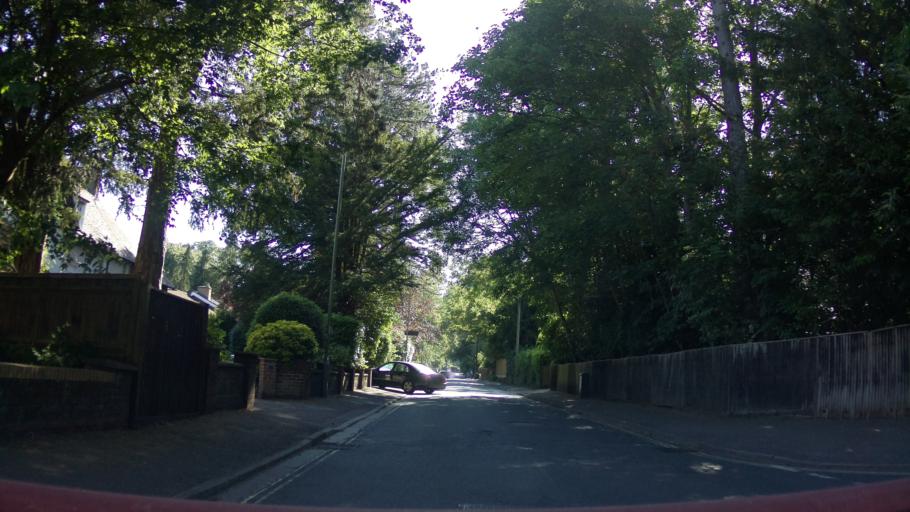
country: GB
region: England
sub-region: Hampshire
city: Winchester
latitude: 51.0711
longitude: -1.3260
